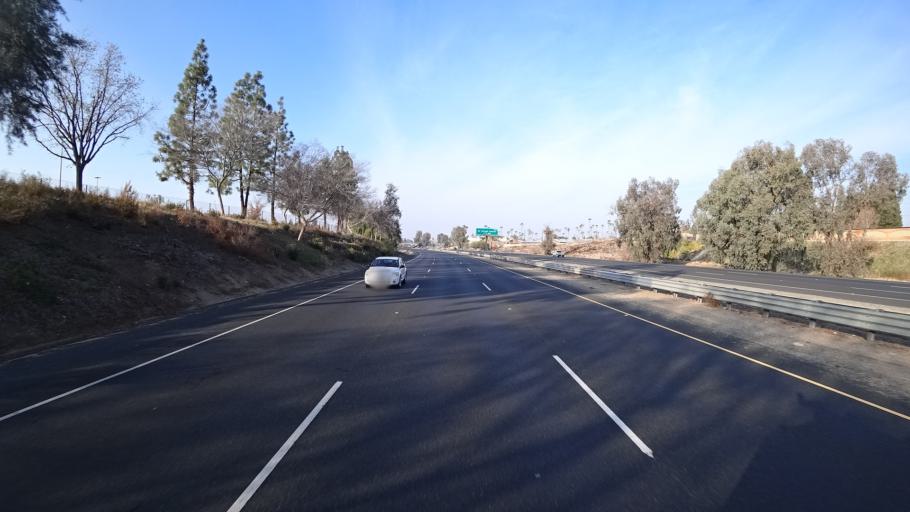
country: US
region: California
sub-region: Kern County
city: Bakersfield
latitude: 35.3961
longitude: -118.9605
